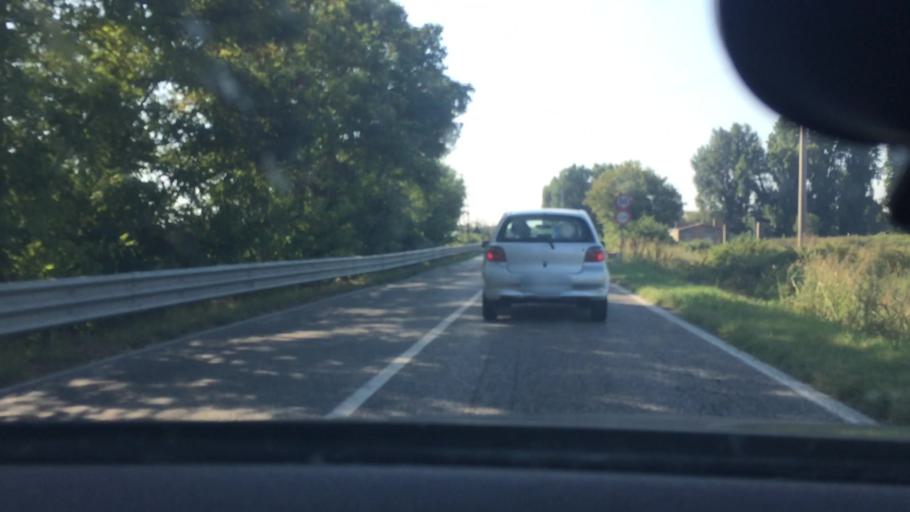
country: IT
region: Emilia-Romagna
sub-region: Provincia di Ferrara
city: Comacchio
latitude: 44.7057
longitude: 12.1639
